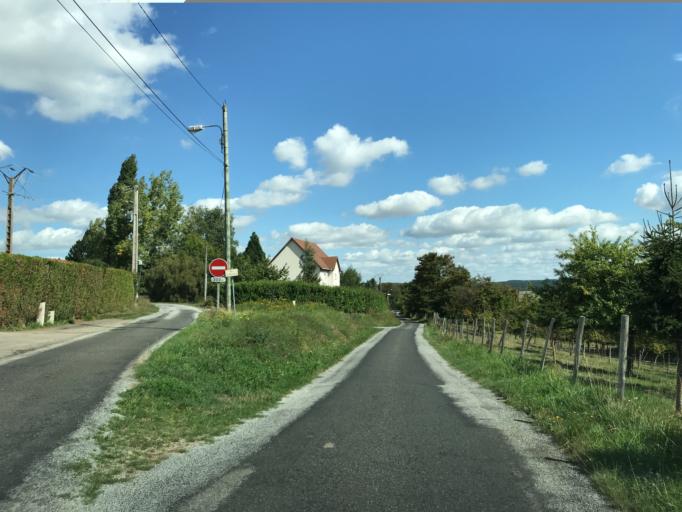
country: FR
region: Haute-Normandie
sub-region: Departement de l'Eure
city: La Chapelle-Reanville
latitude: 49.1364
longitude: 1.3956
